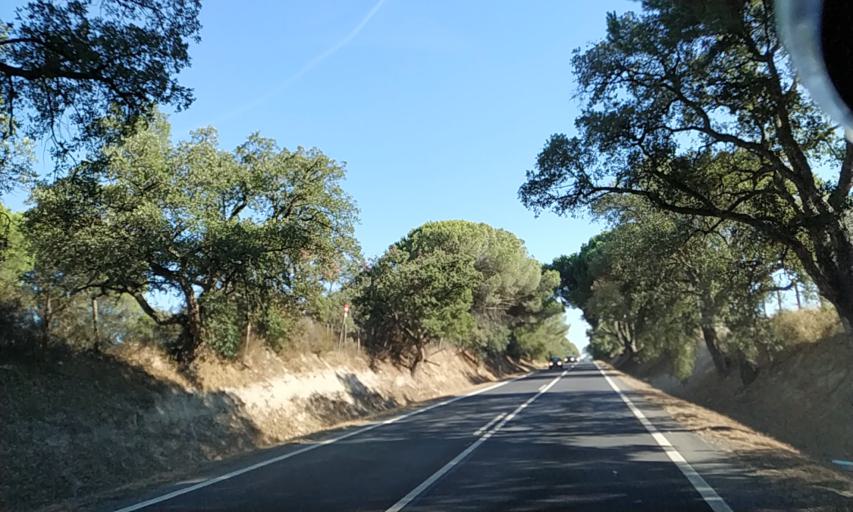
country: PT
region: Santarem
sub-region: Benavente
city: Samora Correia
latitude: 38.8943
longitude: -8.8814
